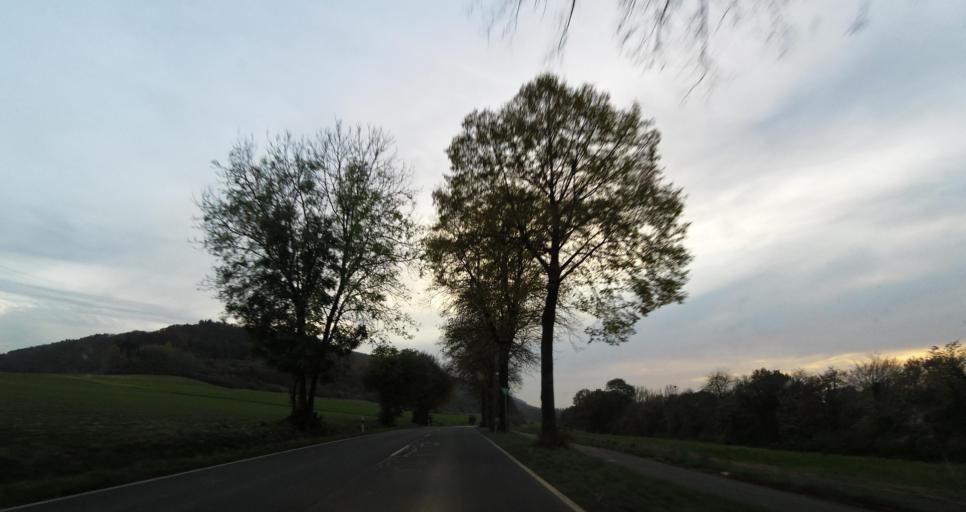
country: DE
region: Lower Saxony
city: Bad Pyrmont
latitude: 51.9851
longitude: 9.3078
